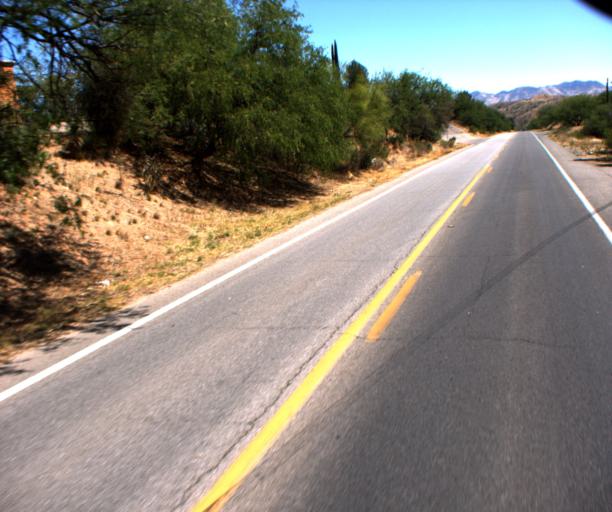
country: US
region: Arizona
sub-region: Santa Cruz County
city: Nogales
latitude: 31.3641
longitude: -110.9039
